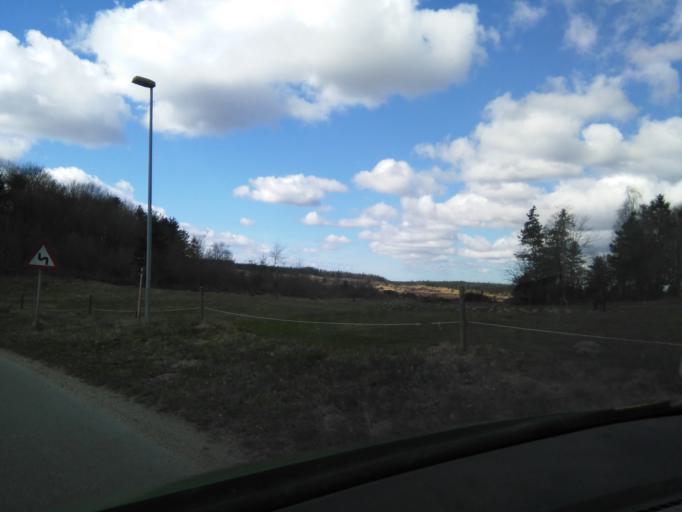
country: DK
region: Central Jutland
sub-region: Silkeborg Kommune
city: Virklund
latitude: 56.0413
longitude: 9.4485
